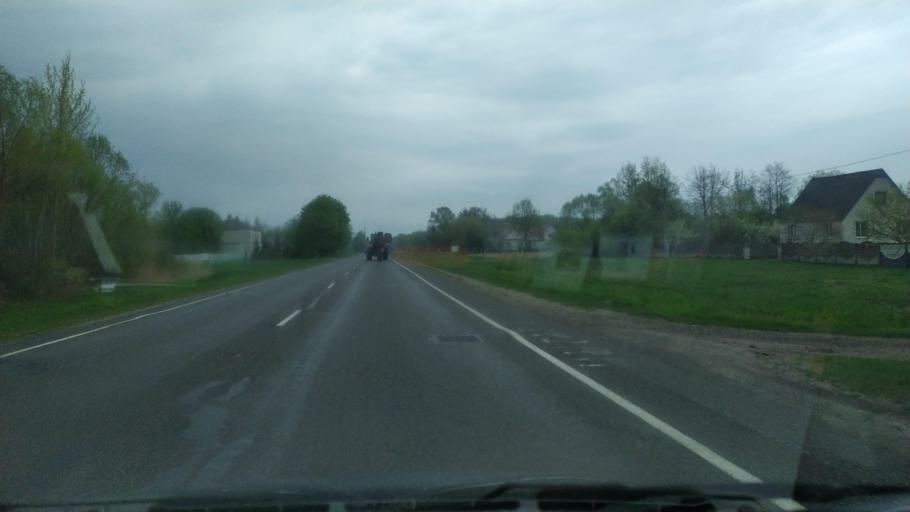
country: BY
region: Brest
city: Horad Kobryn
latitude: 52.3266
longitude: 24.5714
